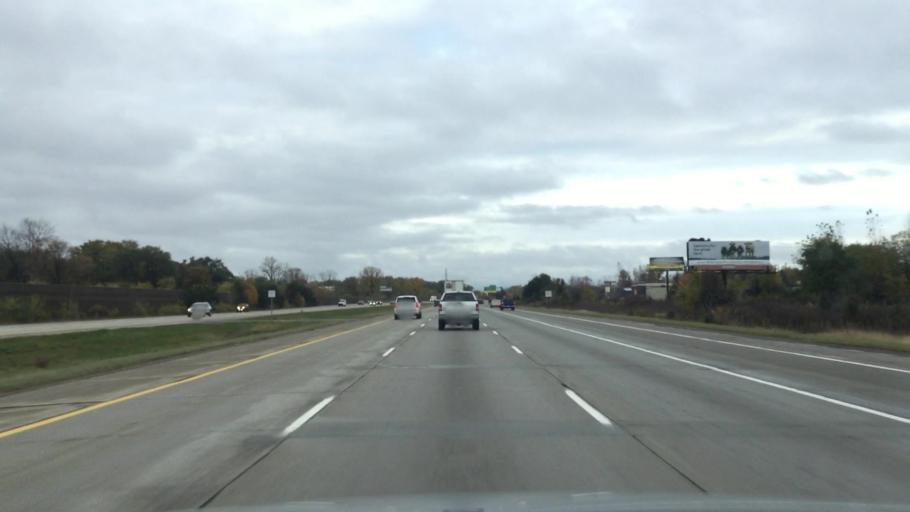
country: US
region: Michigan
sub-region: Wayne County
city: Belleville
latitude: 42.2182
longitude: -83.5497
